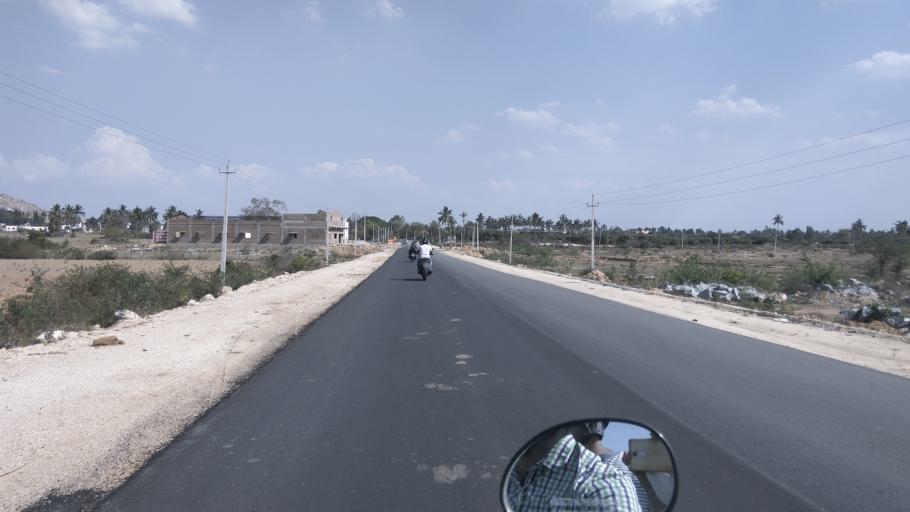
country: IN
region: Karnataka
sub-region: Kolar
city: Mulbagal
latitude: 13.1710
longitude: 78.3591
